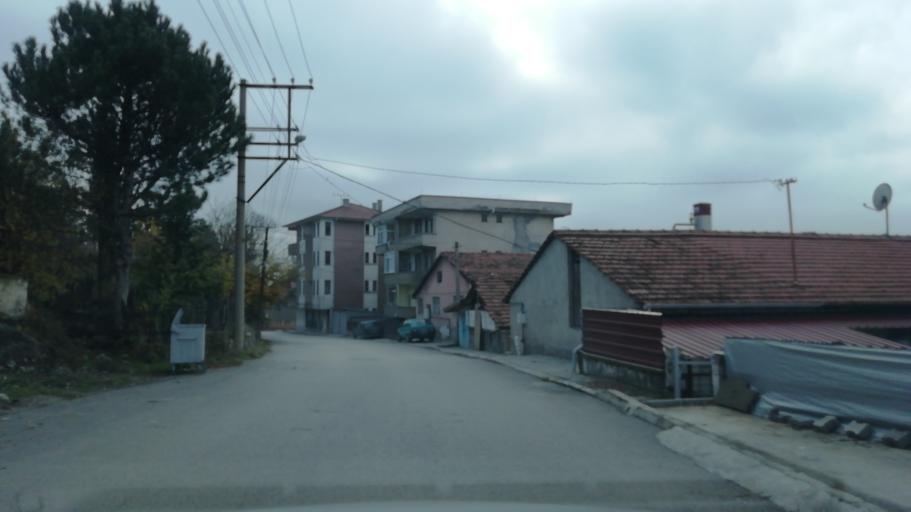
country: TR
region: Karabuk
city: Karabuk
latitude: 41.2173
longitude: 32.6283
